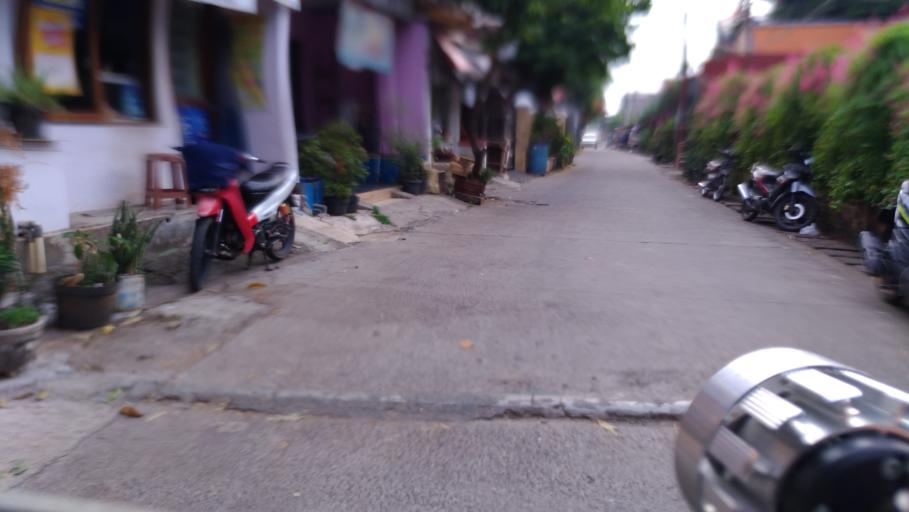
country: ID
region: West Java
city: Depok
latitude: -6.3595
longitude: 106.8693
